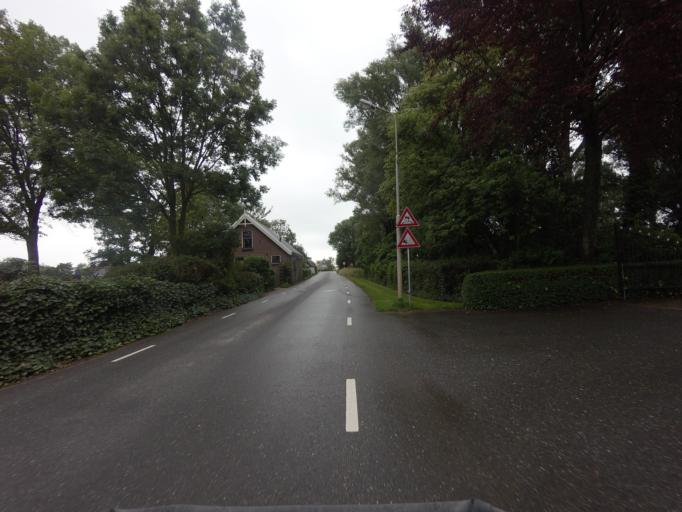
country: NL
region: North Holland
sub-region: Gemeente Schagen
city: Schagen
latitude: 52.7741
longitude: 4.8765
